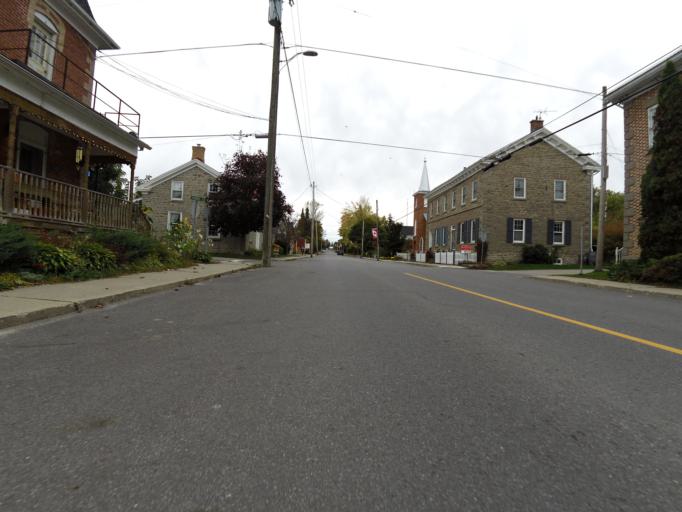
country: CA
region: Ontario
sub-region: Lanark County
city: Smiths Falls
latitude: 44.9126
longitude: -75.8361
